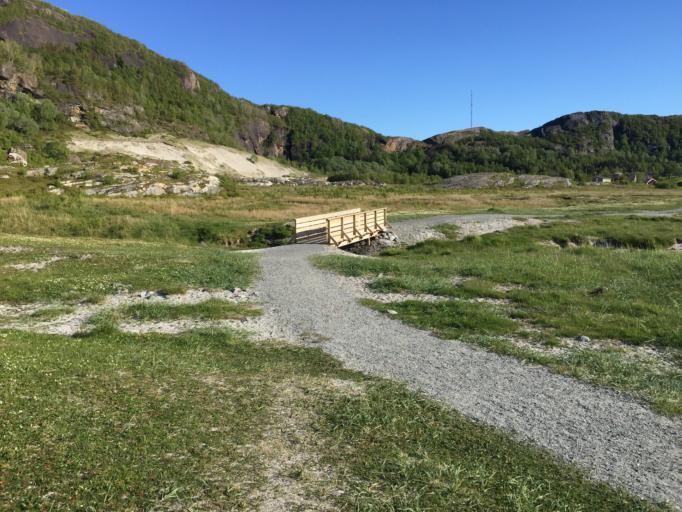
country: NO
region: Nordland
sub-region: Bodo
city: Loding
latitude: 67.4137
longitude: 14.6335
